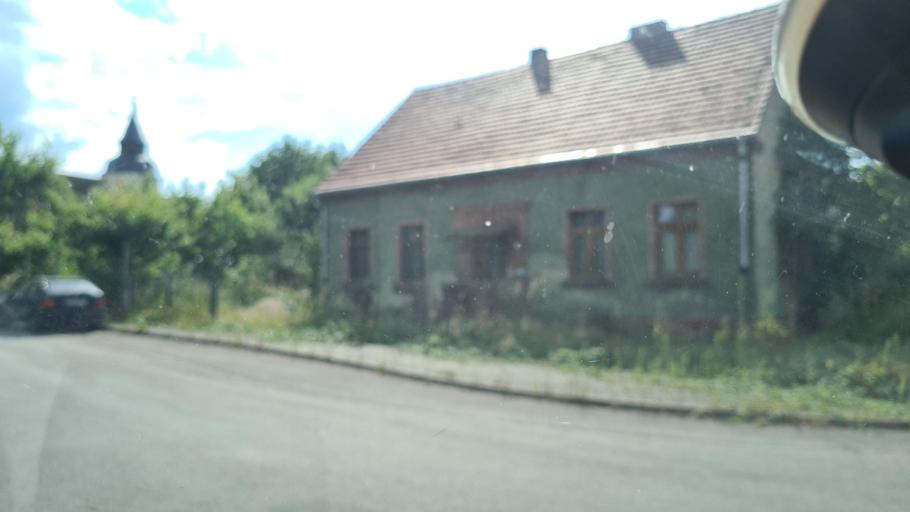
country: DE
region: Brandenburg
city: Neupetershain
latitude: 51.6302
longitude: 14.1302
